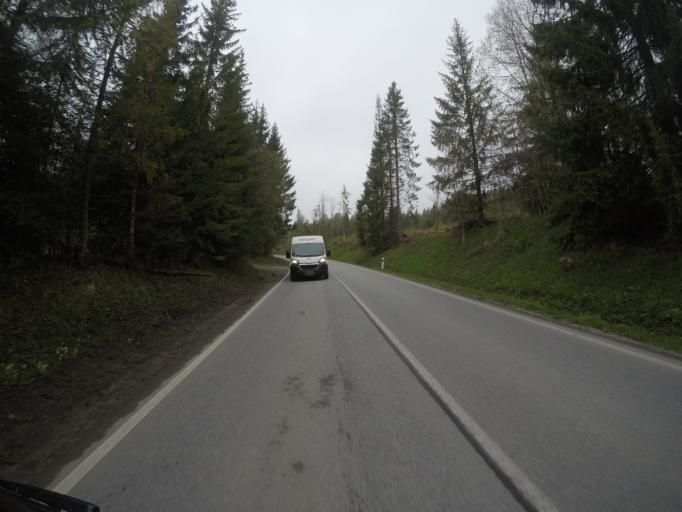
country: SK
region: Presovsky
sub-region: Okres Poprad
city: Strba
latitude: 49.0955
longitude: 20.0679
